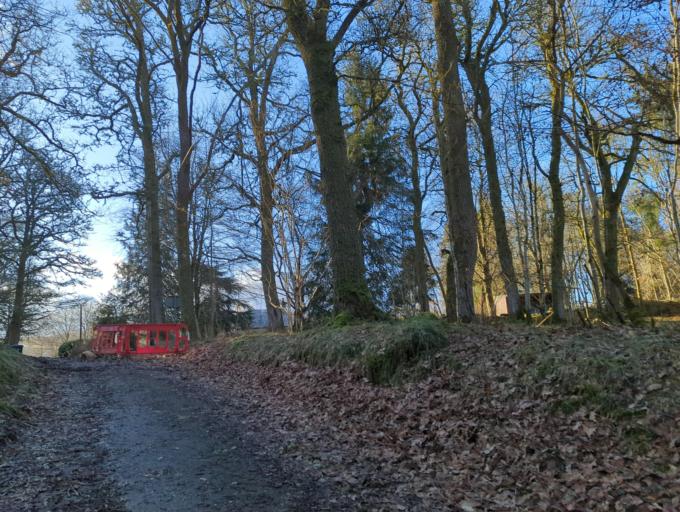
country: GB
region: Scotland
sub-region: Perth and Kinross
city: Bankfoot
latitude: 56.5512
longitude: -3.6341
